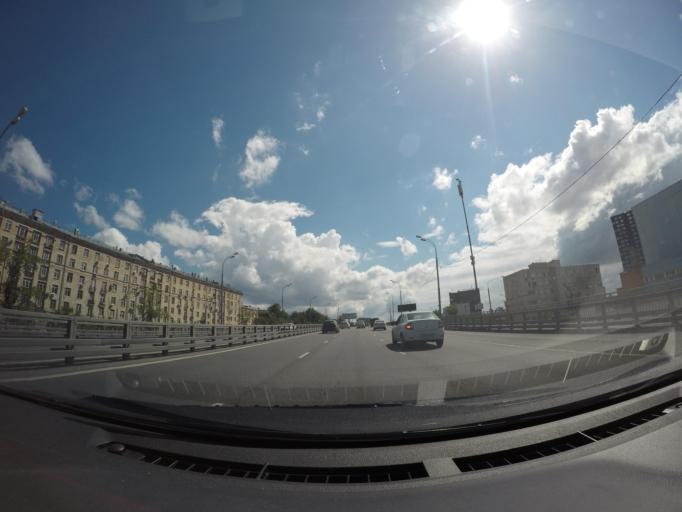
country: RU
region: Moscow
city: Ryazanskiy
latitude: 55.7293
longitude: 37.7491
